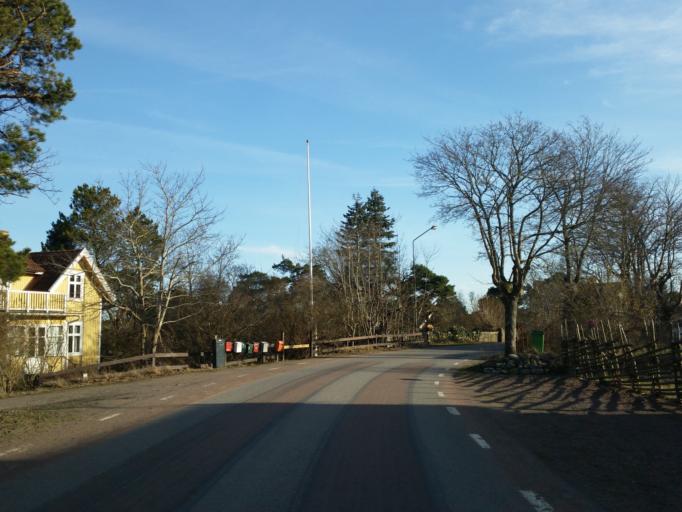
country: SE
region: Kalmar
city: Faerjestaden
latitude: 56.7742
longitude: 16.4760
